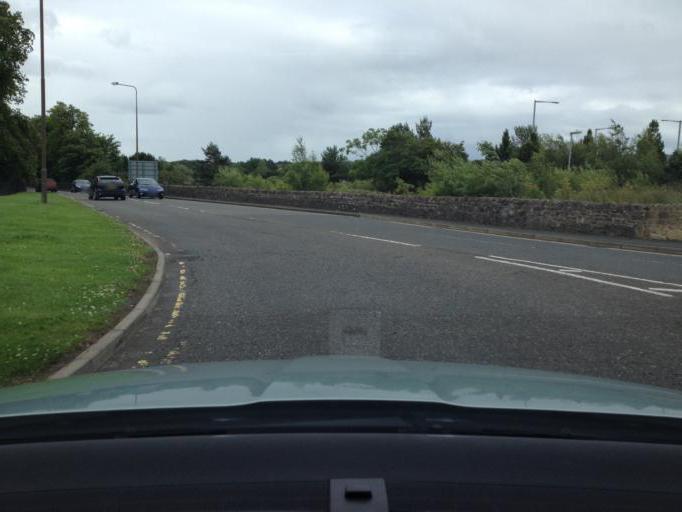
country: GB
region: Scotland
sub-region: West Lothian
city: Livingston
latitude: 55.8883
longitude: -3.5142
